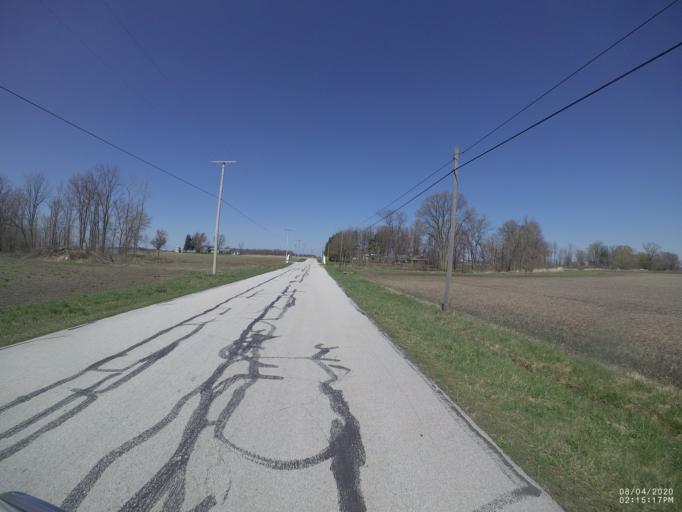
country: US
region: Ohio
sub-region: Sandusky County
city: Gibsonburg
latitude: 41.2803
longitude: -83.2643
